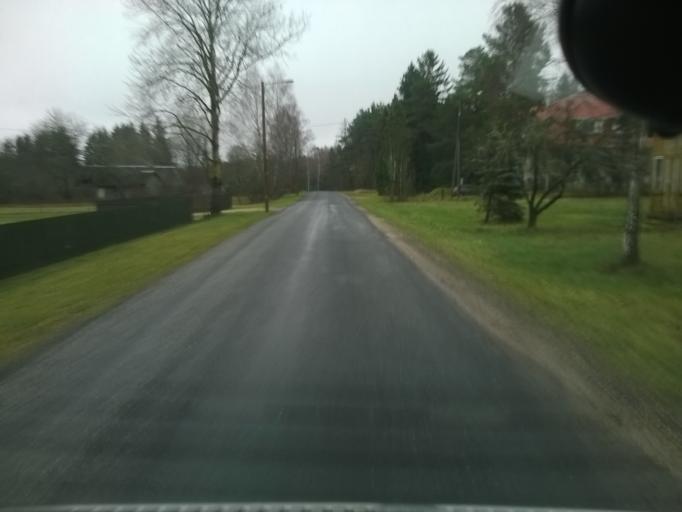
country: EE
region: Harju
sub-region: Nissi vald
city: Riisipere
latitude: 59.1110
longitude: 24.3150
